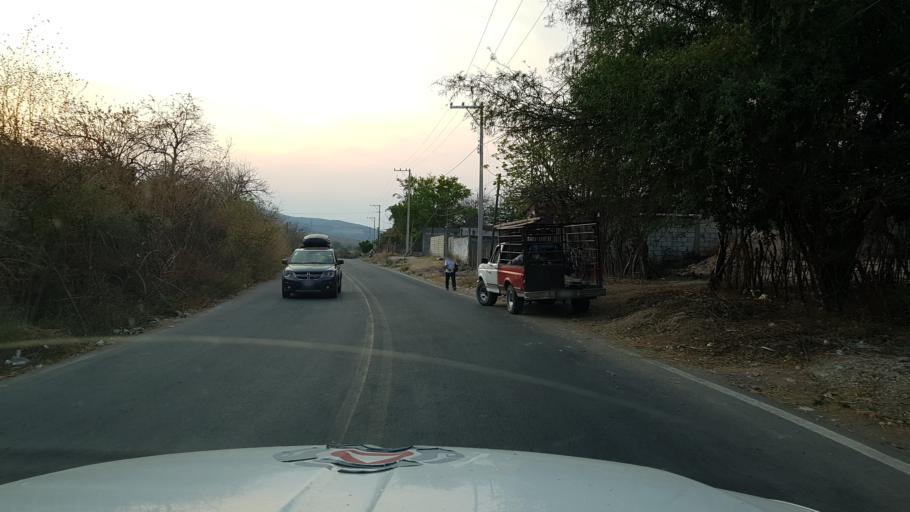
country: MX
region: Morelos
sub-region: Ayala
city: Olintepec
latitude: 18.7296
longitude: -99.0030
